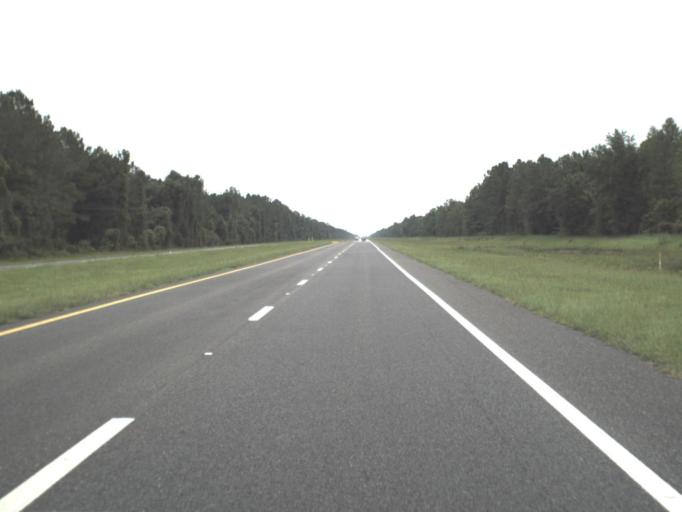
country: US
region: Florida
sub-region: Levy County
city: Chiefland
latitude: 29.3541
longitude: -82.7847
